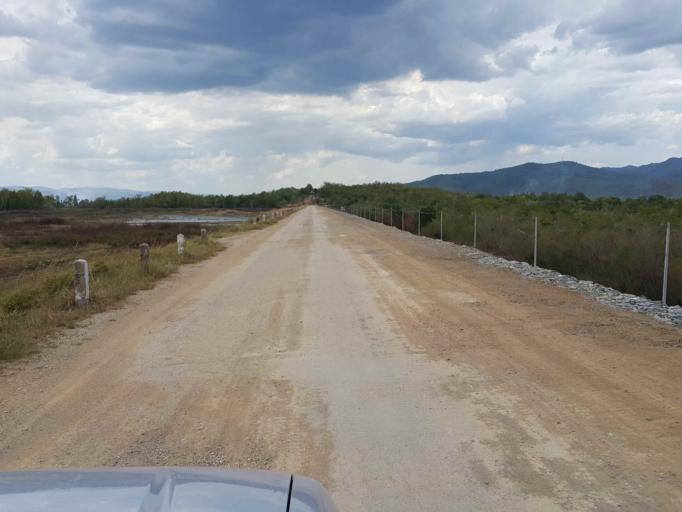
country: TH
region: Sukhothai
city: Thung Saliam
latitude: 17.3187
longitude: 99.4238
